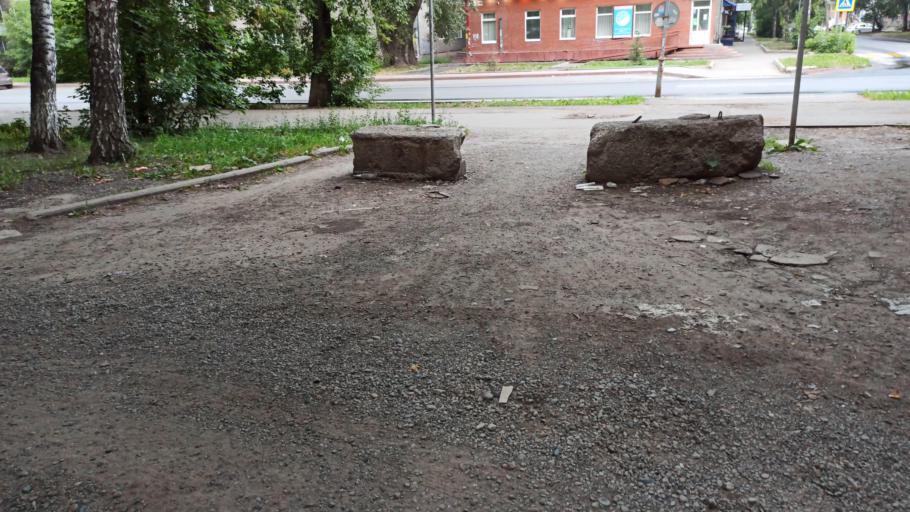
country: RU
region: Tomsk
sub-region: Tomskiy Rayon
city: Tomsk
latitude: 56.4636
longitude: 84.9697
